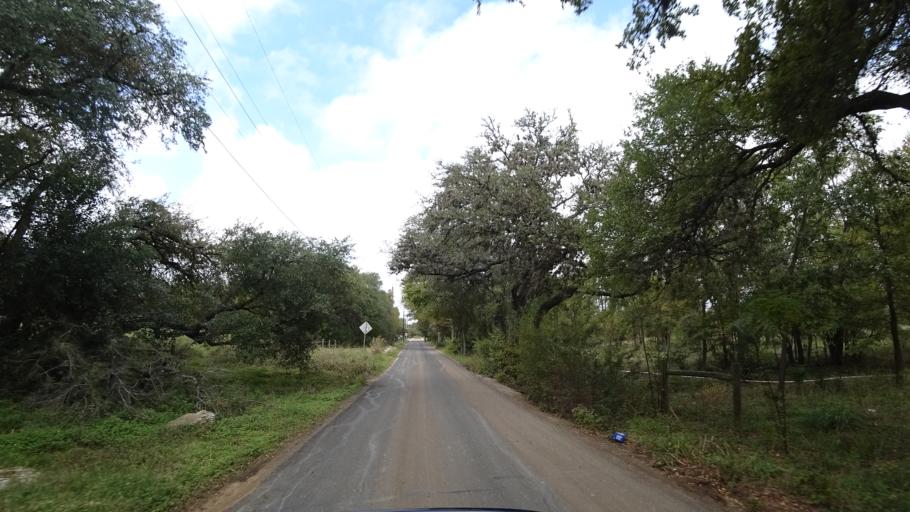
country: US
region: Texas
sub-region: Travis County
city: Shady Hollow
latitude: 30.2085
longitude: -97.8318
